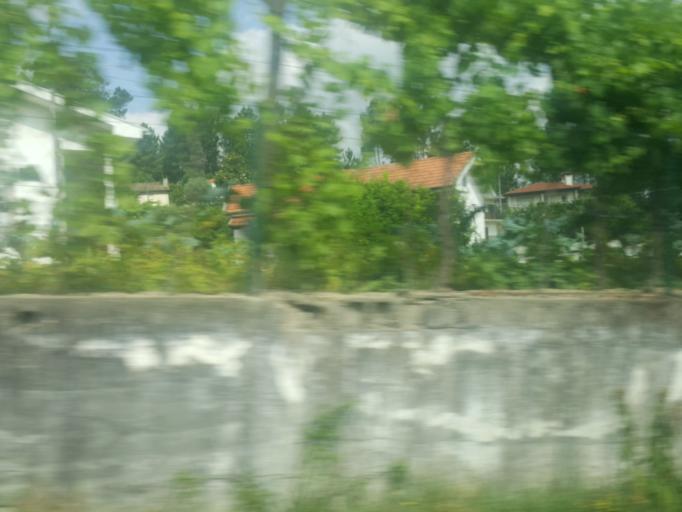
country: PT
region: Porto
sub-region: Marco de Canaveses
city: Marco de Canavezes
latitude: 41.1995
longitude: -8.1658
